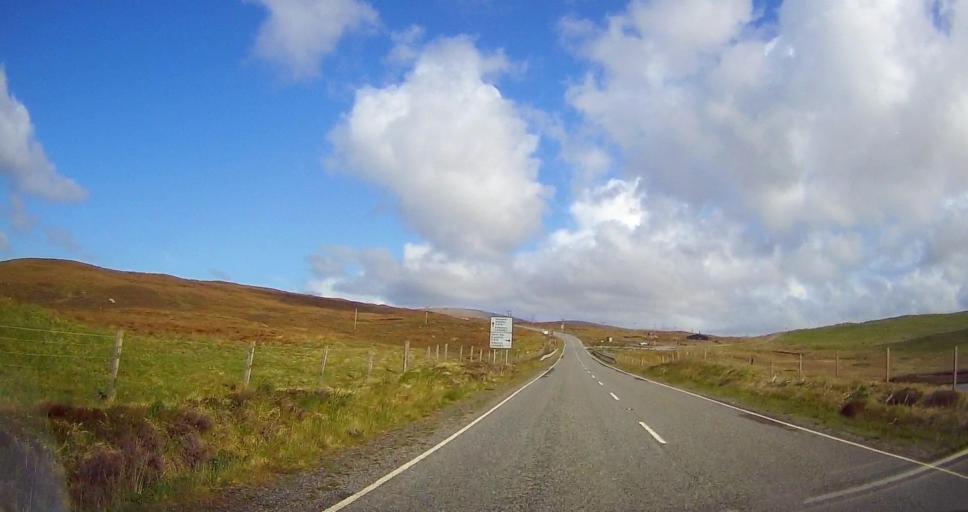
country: GB
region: Scotland
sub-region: Shetland Islands
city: Lerwick
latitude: 60.4740
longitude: -1.4077
